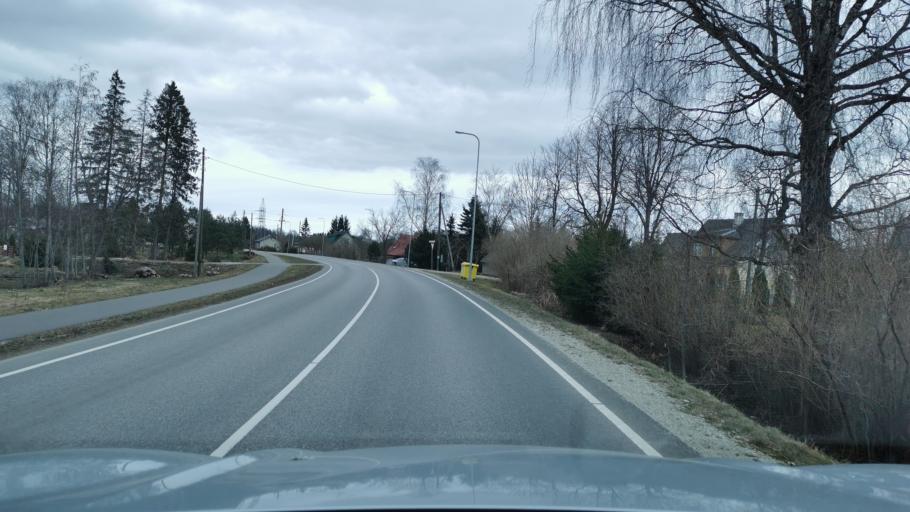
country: EE
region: Ida-Virumaa
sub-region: Puessi linn
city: Pussi
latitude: 59.3435
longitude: 27.0153
